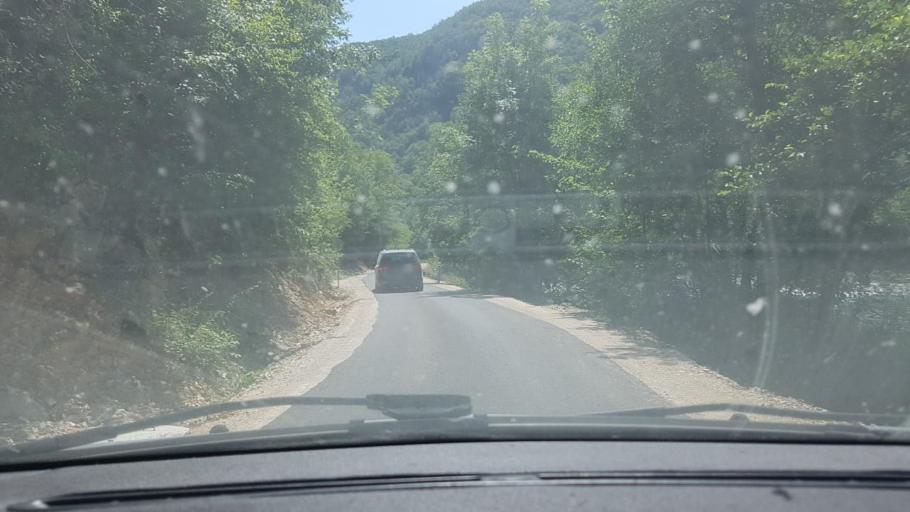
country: BA
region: Federation of Bosnia and Herzegovina
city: Orasac
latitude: 44.6323
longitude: 16.0435
